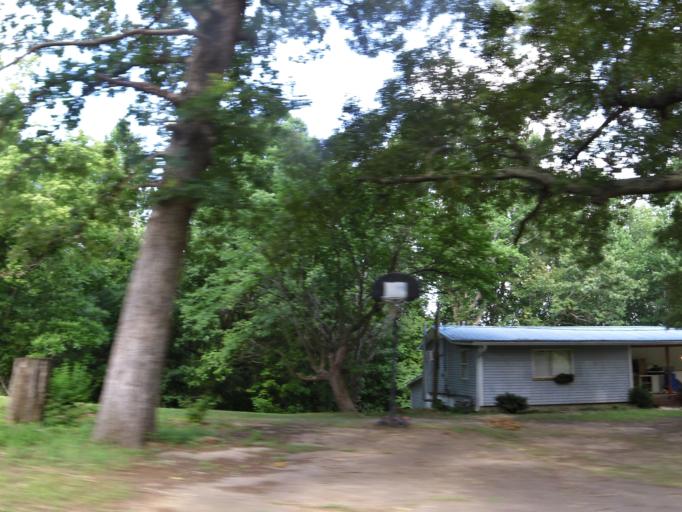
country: US
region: Tennessee
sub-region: Benton County
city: Camden
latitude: 36.0521
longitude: -88.1665
